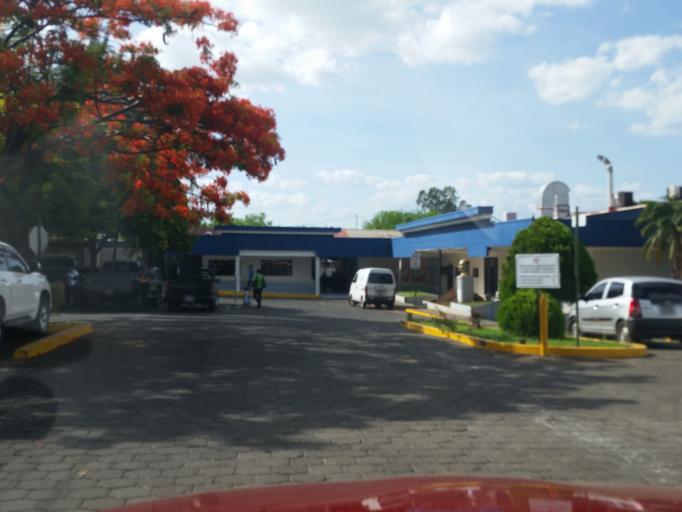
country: NI
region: Managua
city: Managua
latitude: 12.1414
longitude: -86.2625
